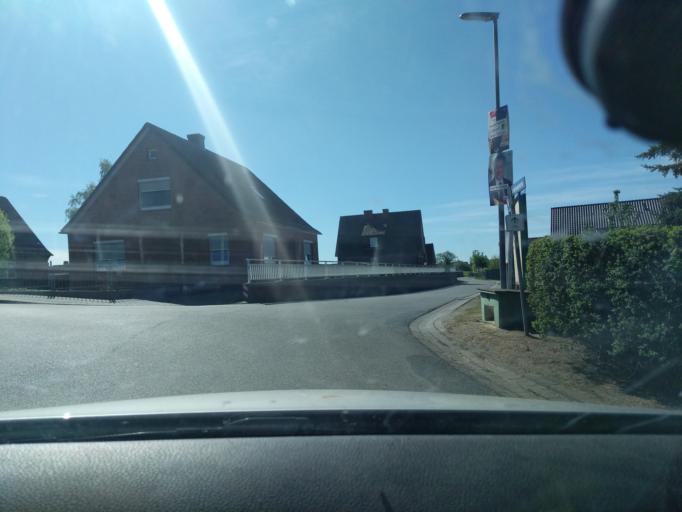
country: DE
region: Lower Saxony
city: Neuenkirchen
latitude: 53.5275
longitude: 9.6043
